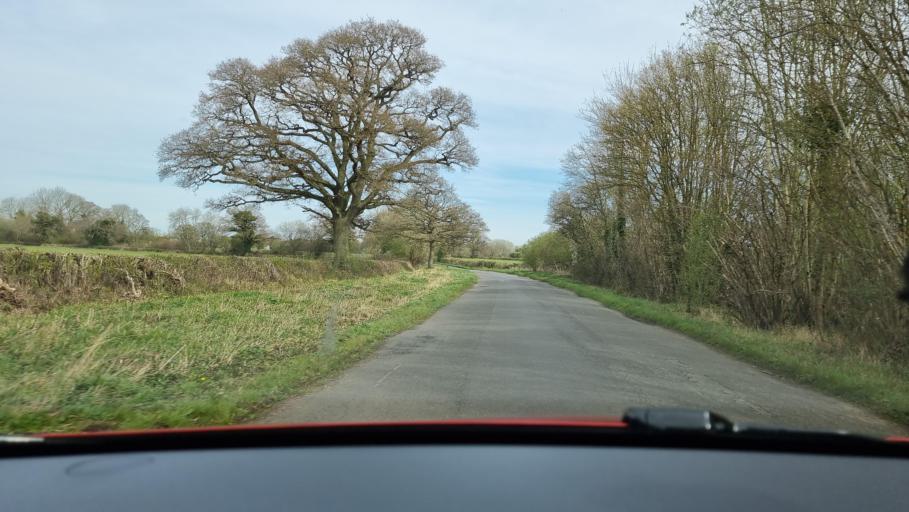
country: GB
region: England
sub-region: Oxfordshire
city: Kidlington
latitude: 51.8596
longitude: -1.2446
